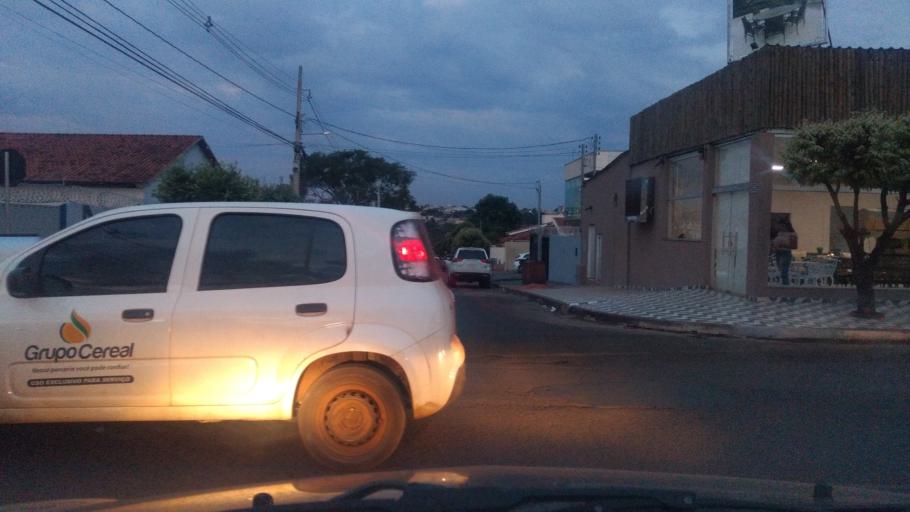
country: BR
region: Goias
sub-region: Santa Helena De Goias
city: Santa Helena de Goias
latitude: -17.7924
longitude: -50.9438
